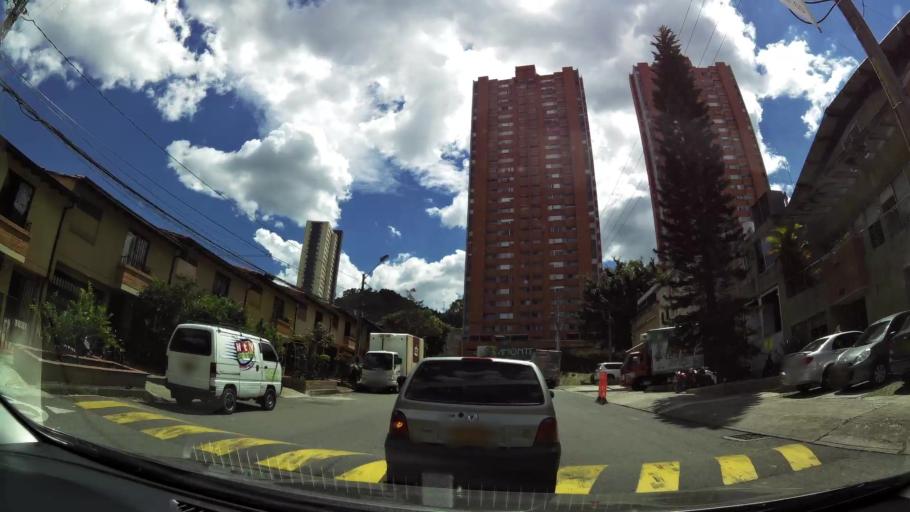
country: CO
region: Antioquia
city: Sabaneta
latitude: 6.1475
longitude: -75.6252
